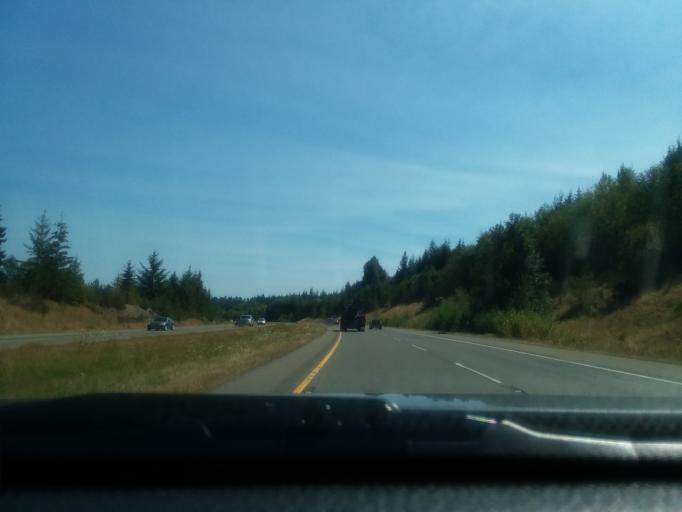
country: CA
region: British Columbia
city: Port Alberni
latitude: 49.4618
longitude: -124.7985
